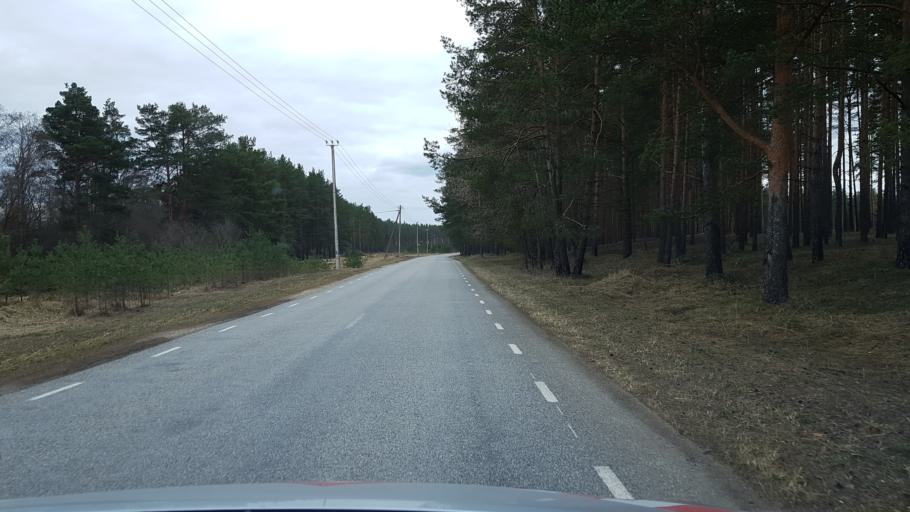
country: EE
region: Ida-Virumaa
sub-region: Narva-Joesuu linn
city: Narva-Joesuu
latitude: 59.4263
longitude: 28.1200
